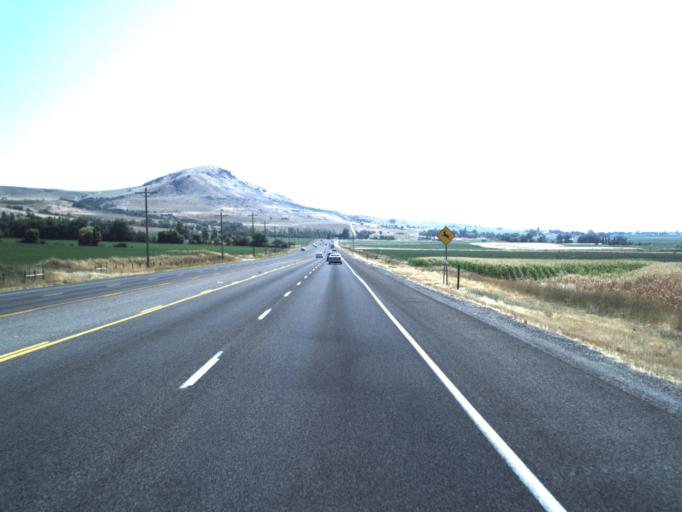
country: US
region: Utah
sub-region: Cache County
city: Richmond
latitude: 41.9050
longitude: -111.8148
